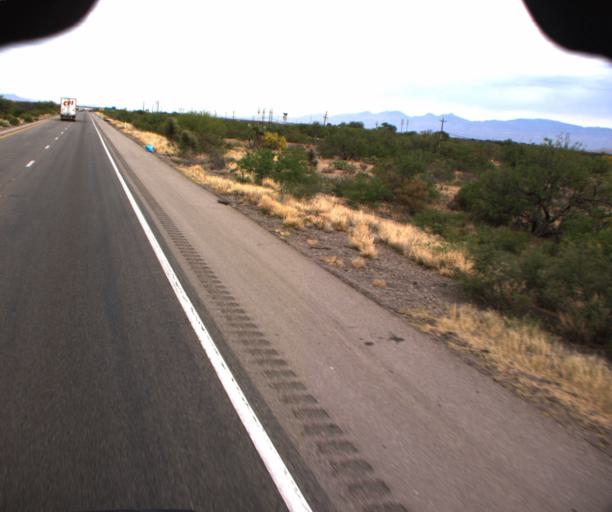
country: US
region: Arizona
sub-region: Pima County
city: Vail
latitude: 32.0230
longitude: -110.7129
